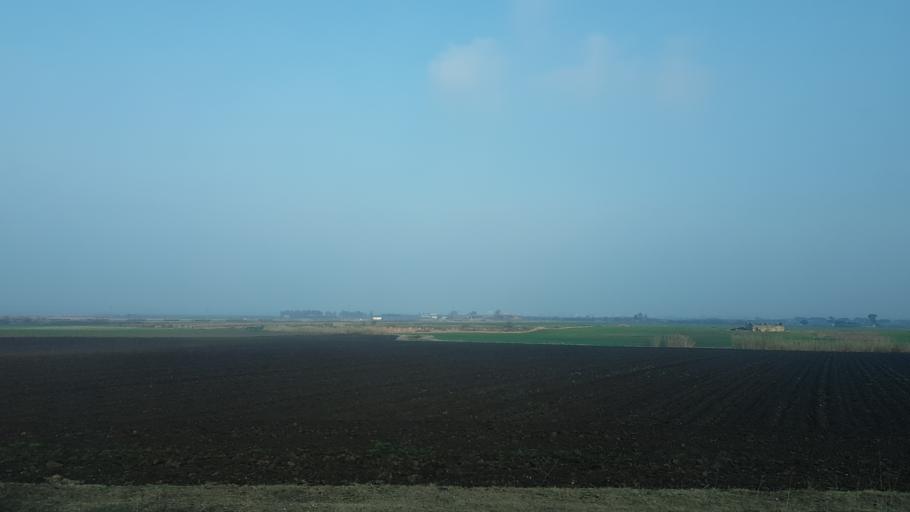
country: IT
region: Apulia
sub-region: Provincia di Foggia
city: Lesina
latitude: 41.8640
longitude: 15.2957
